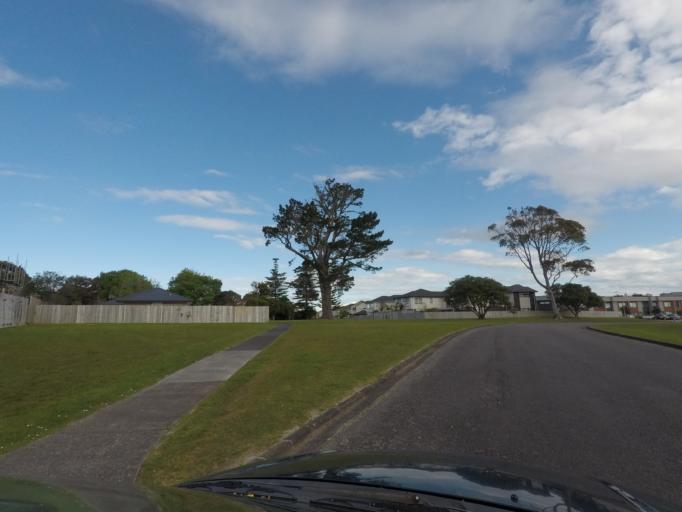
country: NZ
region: Auckland
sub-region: Auckland
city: Rosebank
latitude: -36.8726
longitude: 174.6440
